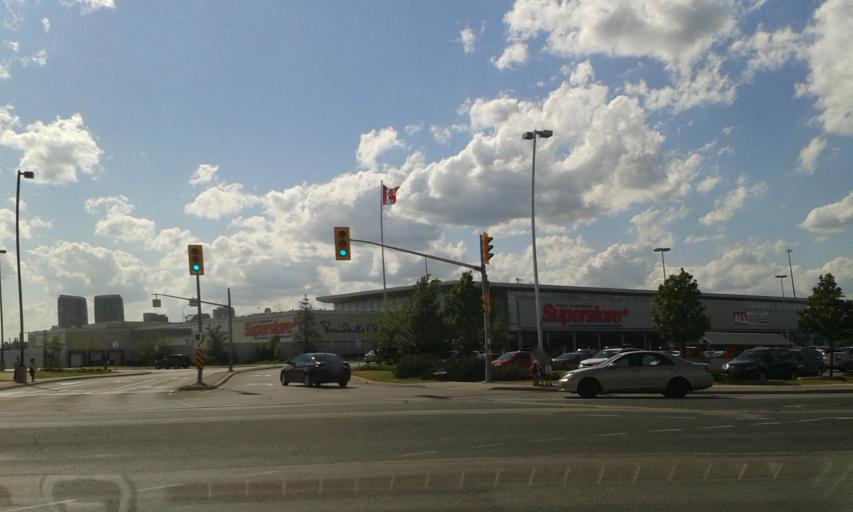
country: CA
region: Ontario
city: Scarborough
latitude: 43.7773
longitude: -79.2609
